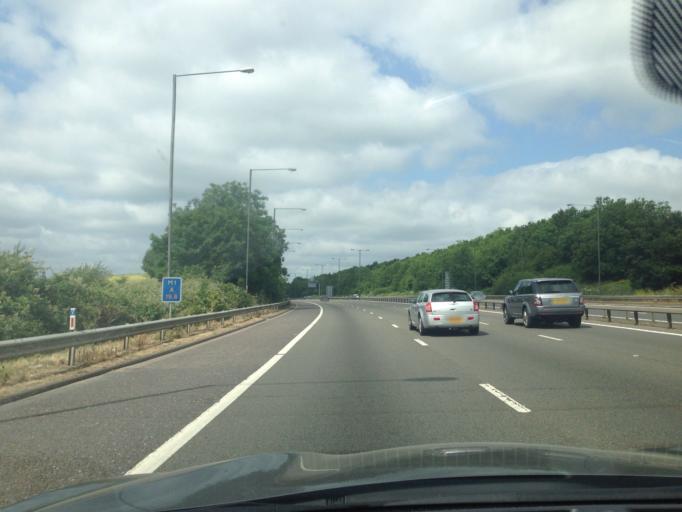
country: GB
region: England
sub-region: Hertfordshire
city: Borehamwood
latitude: 51.6380
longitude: -0.2777
